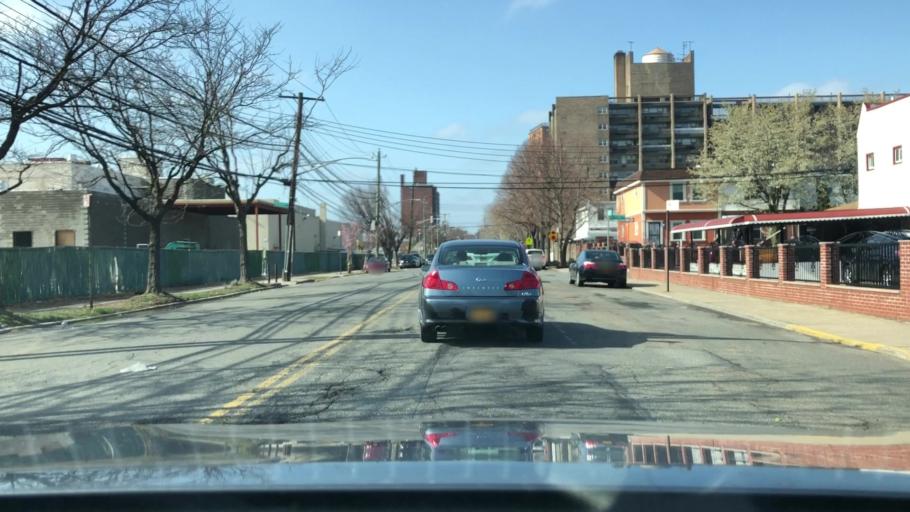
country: US
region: New York
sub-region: Bronx
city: The Bronx
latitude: 40.8235
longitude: -73.8554
